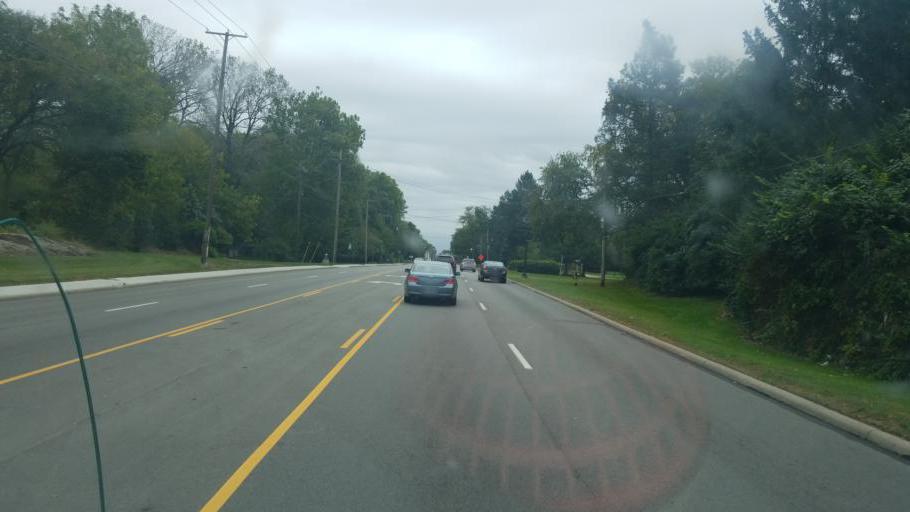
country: US
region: Ohio
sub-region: Lucas County
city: Ottawa Hills
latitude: 41.6770
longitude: -83.6527
